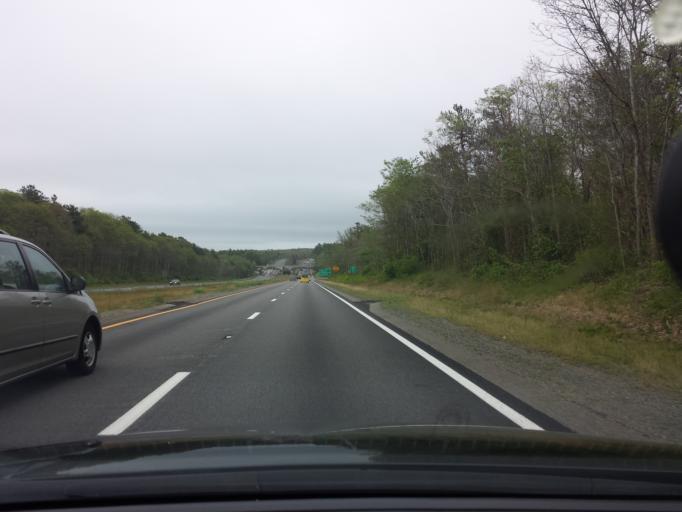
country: US
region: Massachusetts
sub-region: Barnstable County
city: East Sandwich
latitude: 41.7195
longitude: -70.4256
